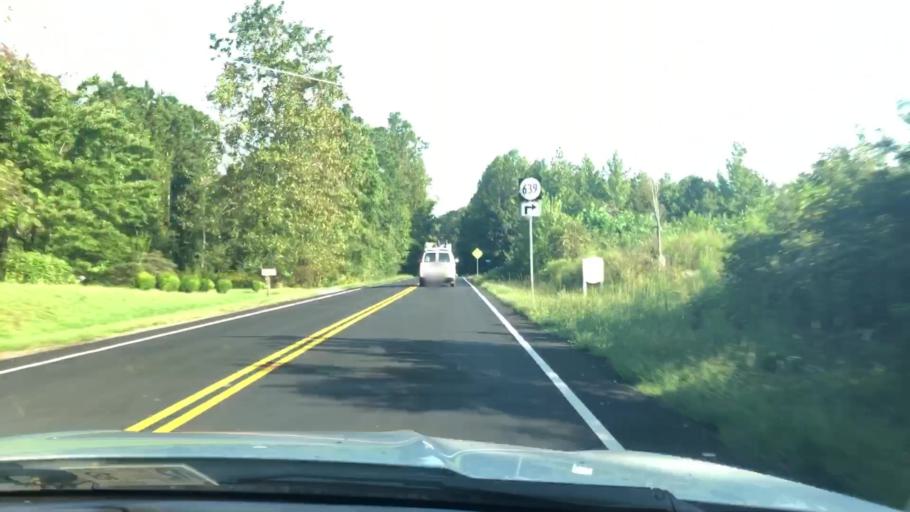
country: US
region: Virginia
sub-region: King William County
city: West Point
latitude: 37.4750
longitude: -76.8460
